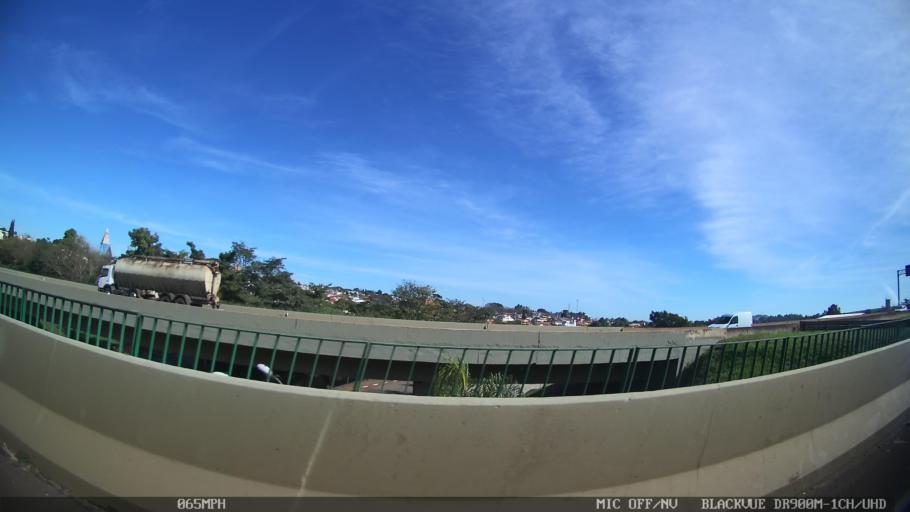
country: BR
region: Sao Paulo
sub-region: Araras
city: Araras
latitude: -22.3489
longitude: -47.3945
